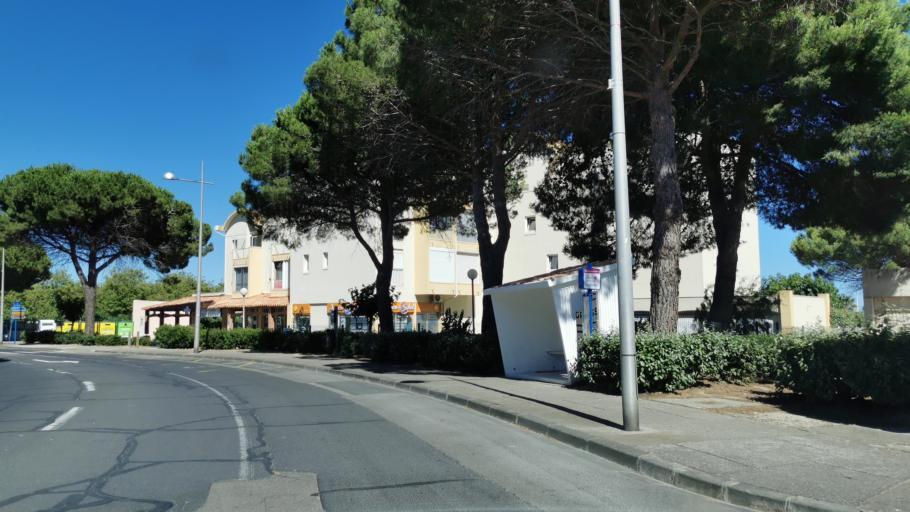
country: FR
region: Languedoc-Roussillon
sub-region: Departement de l'Aude
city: Gruissan
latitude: 43.1107
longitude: 3.1013
